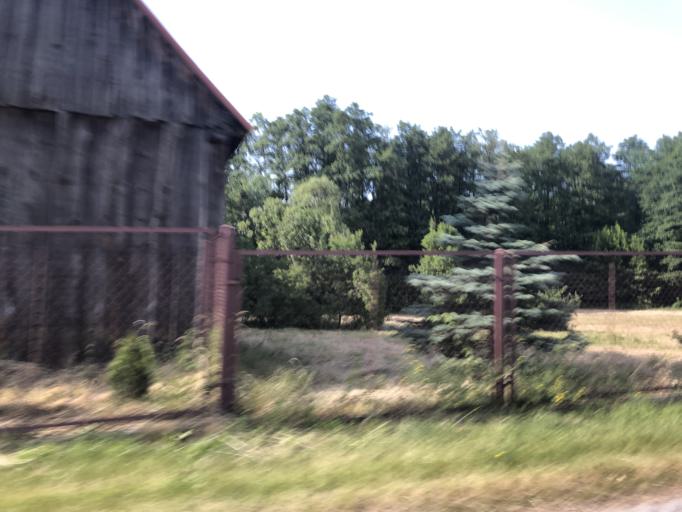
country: PL
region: Podlasie
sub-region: Lomza
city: Lomza
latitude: 53.1445
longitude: 22.0079
